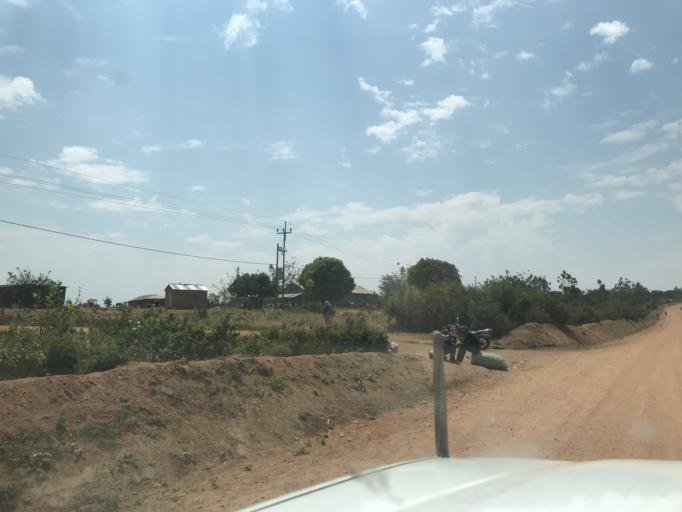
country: TZ
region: Mara
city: Nyamuswa
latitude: -1.9428
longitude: 33.9920
